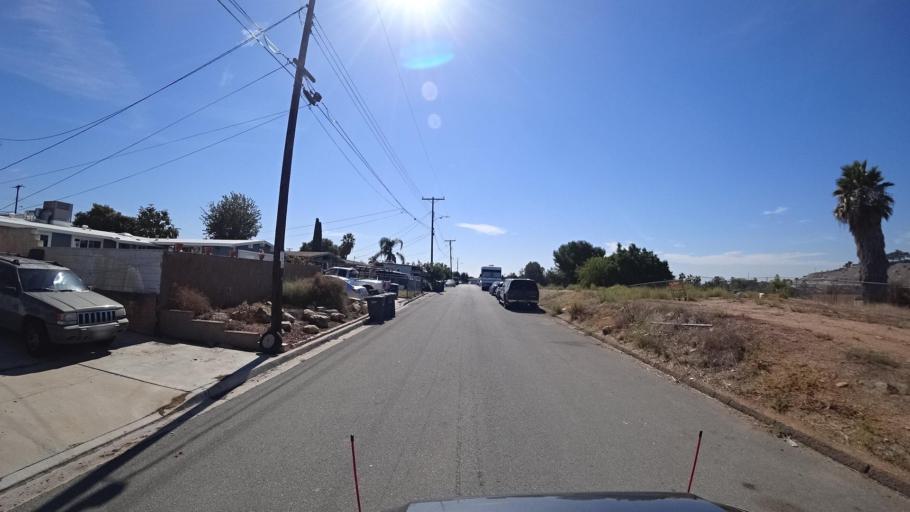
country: US
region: California
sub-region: San Diego County
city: La Presa
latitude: 32.7022
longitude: -117.0050
